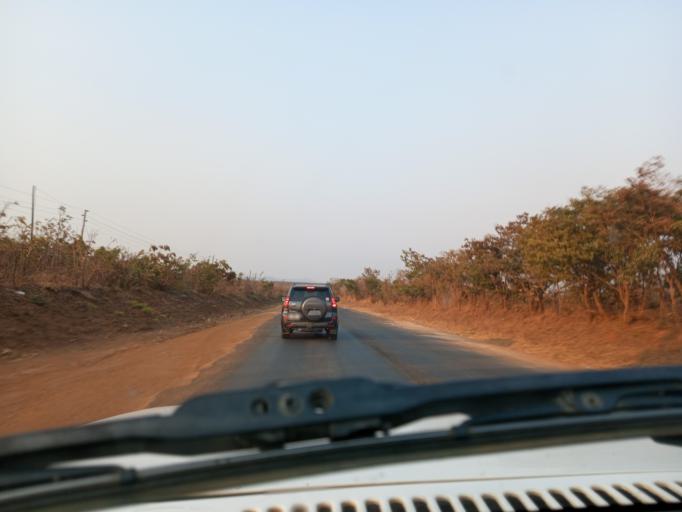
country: ZM
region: Northern
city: Mpika
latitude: -11.8944
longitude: 31.4170
